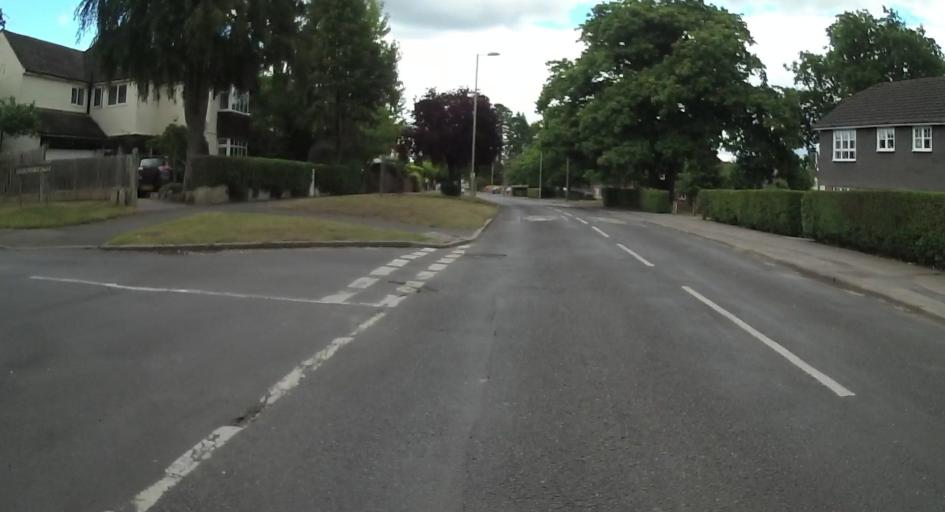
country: GB
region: England
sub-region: Hampshire
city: Aldershot
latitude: 51.2378
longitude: -0.7667
